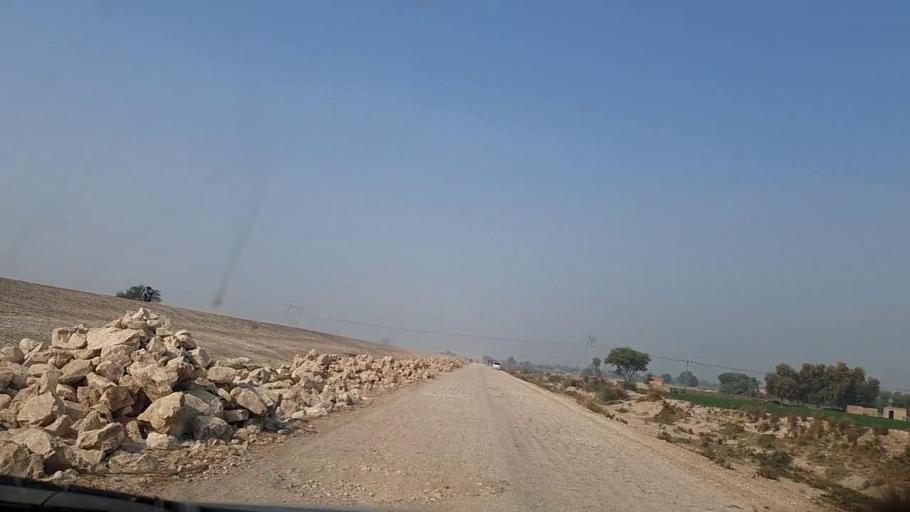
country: PK
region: Sindh
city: Moro
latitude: 26.7072
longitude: 67.9257
